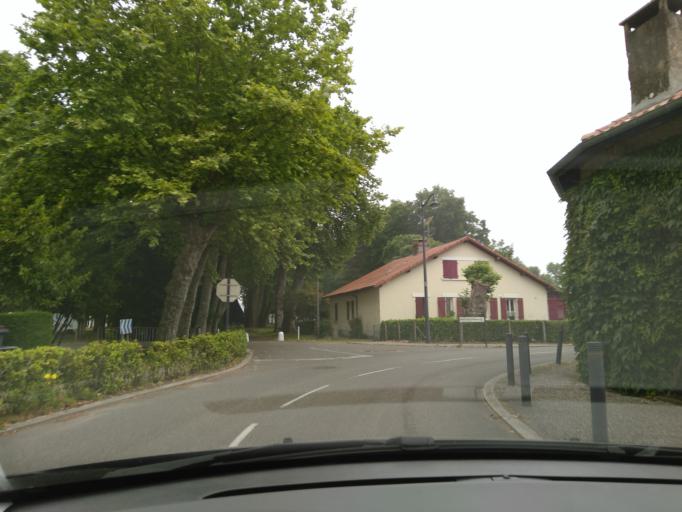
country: FR
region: Aquitaine
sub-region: Departement des Landes
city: Saint-Vincent-de-Paul
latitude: 43.7846
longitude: -0.9896
